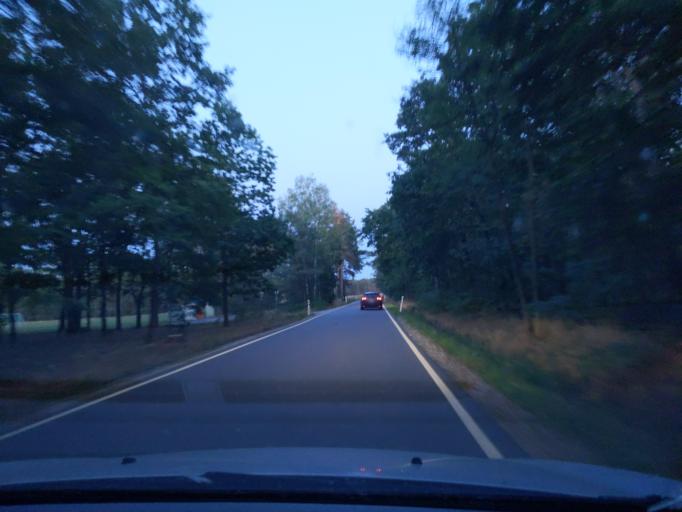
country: DE
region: Saxony
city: Lohsa
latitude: 51.3302
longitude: 14.3924
